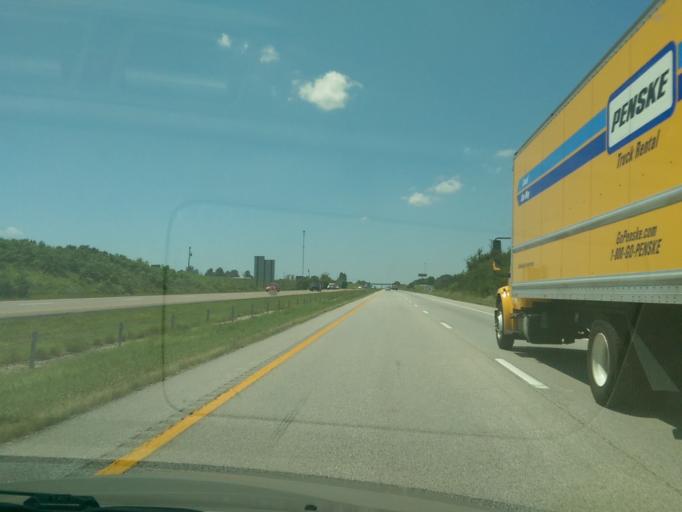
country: US
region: Missouri
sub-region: Cooper County
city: Boonville
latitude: 38.9353
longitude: -92.8039
